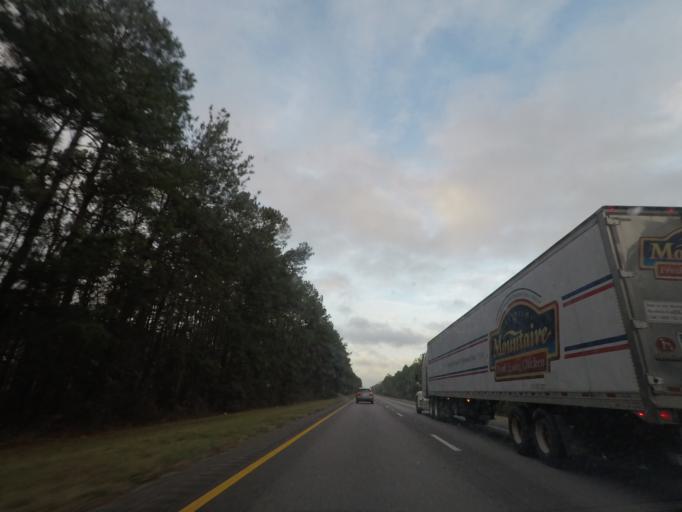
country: US
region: South Carolina
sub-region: Orangeburg County
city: Holly Hill
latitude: 33.3314
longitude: -80.5392
